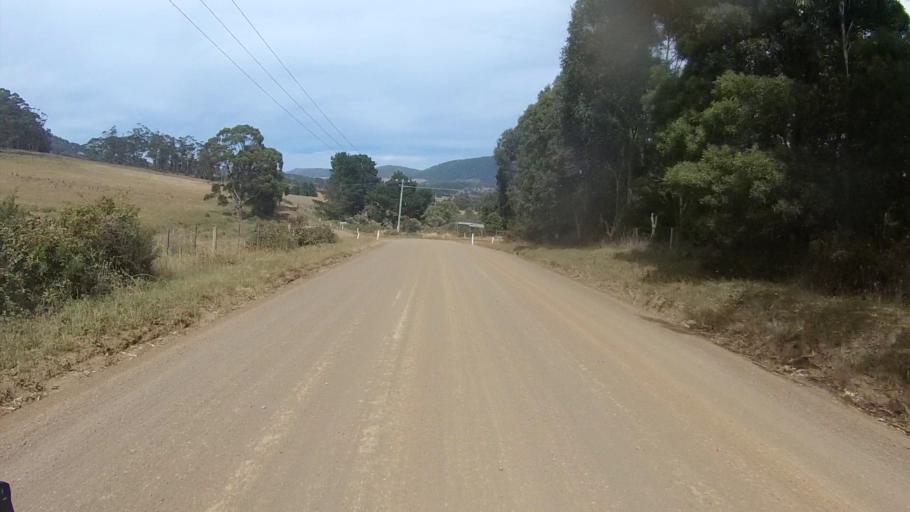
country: AU
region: Tasmania
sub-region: Sorell
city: Sorell
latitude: -42.7801
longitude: 147.8115
